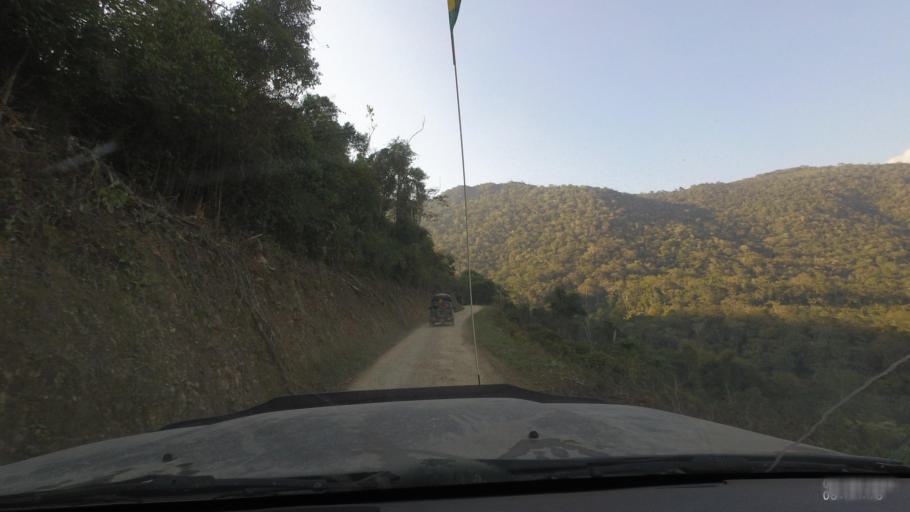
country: BO
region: La Paz
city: Quime
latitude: -16.5044
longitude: -66.7628
